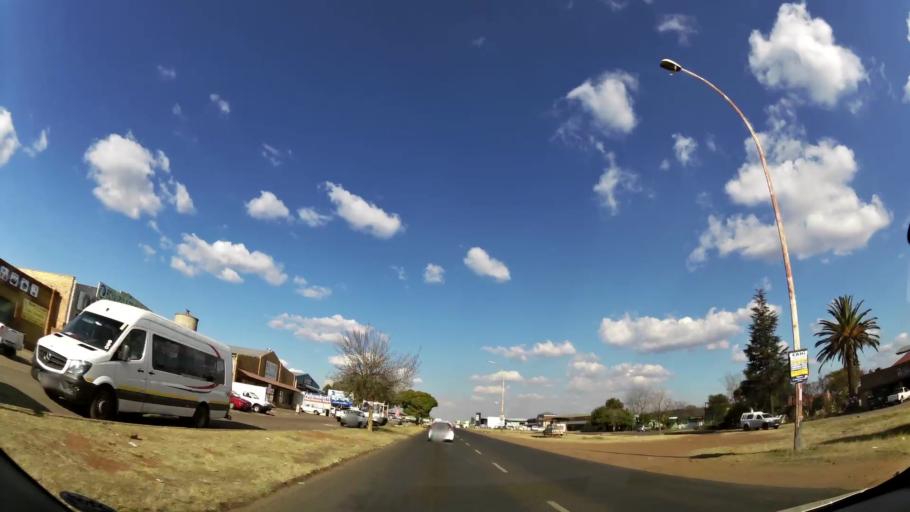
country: ZA
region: Mpumalanga
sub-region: Nkangala District Municipality
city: Witbank
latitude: -25.8921
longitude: 29.2265
